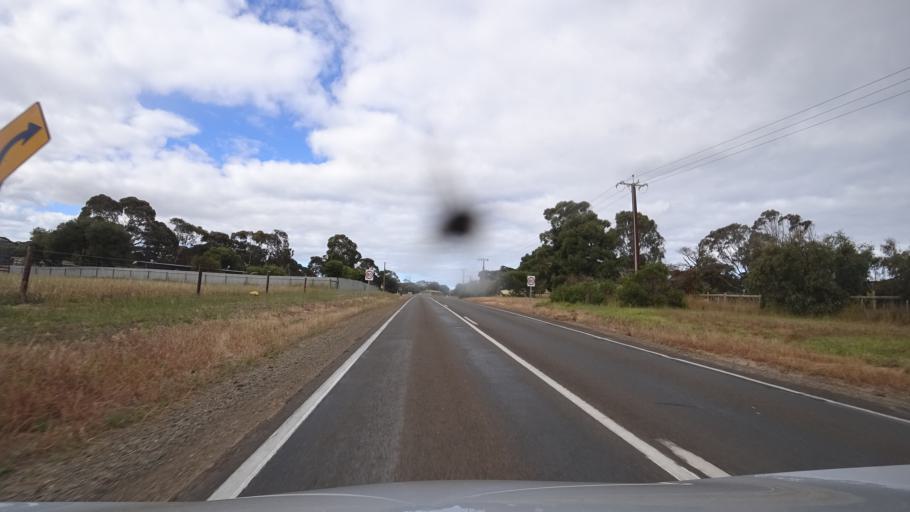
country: AU
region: South Australia
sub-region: Kangaroo Island
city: Kingscote
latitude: -35.6632
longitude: 137.5993
